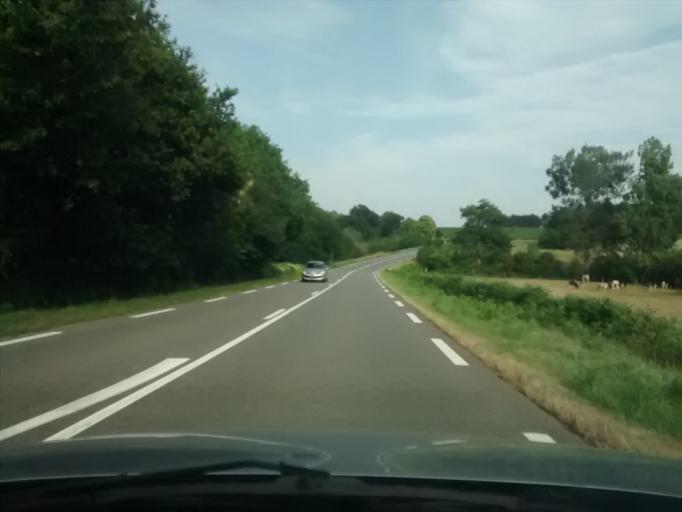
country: FR
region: Brittany
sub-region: Departement d'Ille-et-Vilaine
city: Erbree
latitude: 48.1114
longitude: -1.1182
